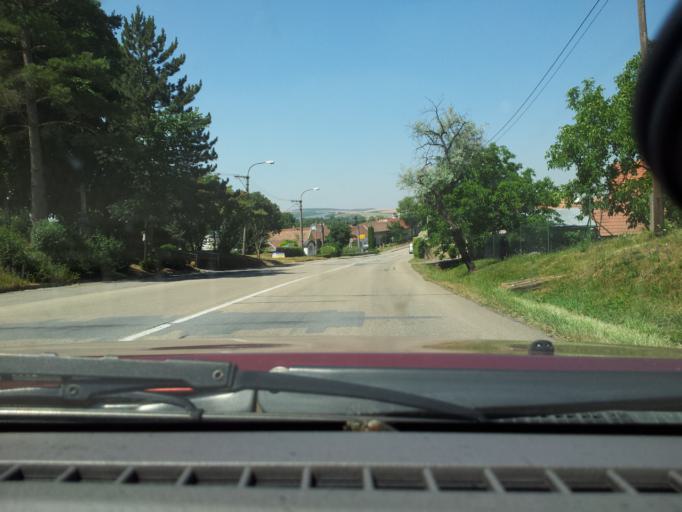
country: CZ
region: South Moravian
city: Cejc
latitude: 48.9534
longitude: 16.9450
